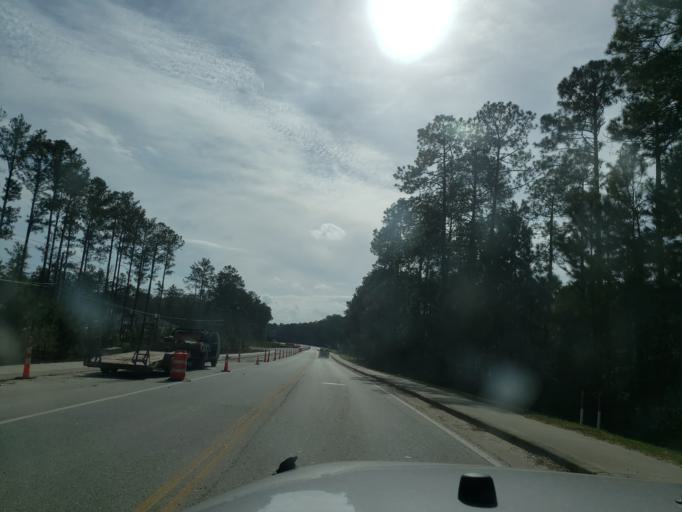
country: US
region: Georgia
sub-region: Chatham County
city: Pooler
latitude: 32.1724
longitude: -81.2336
